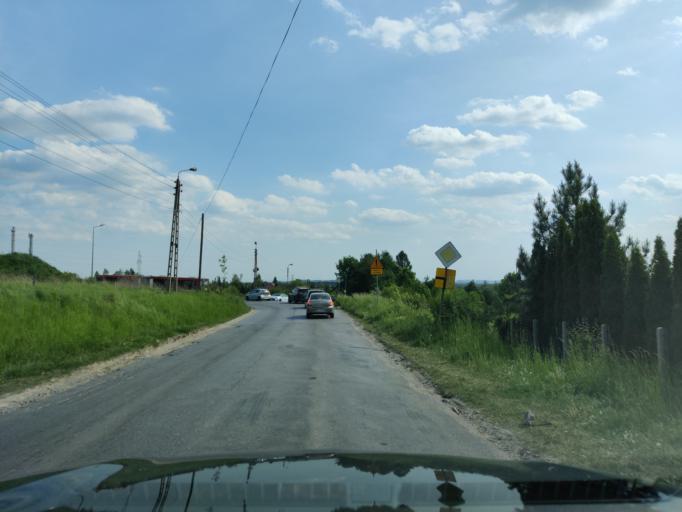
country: PL
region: Silesian Voivodeship
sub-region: Dabrowa Gornicza
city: Dabrowa Gornicza
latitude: 50.3862
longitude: 19.2420
